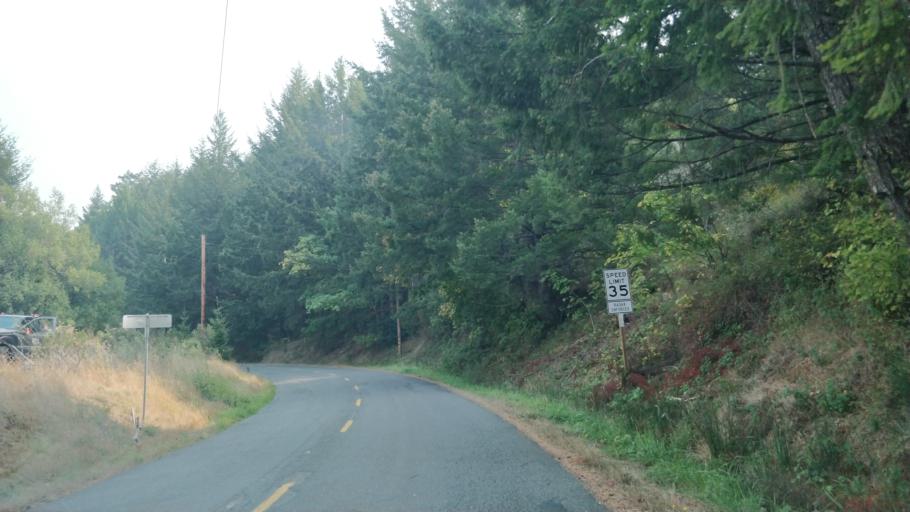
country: US
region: California
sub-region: Humboldt County
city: Rio Dell
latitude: 40.3127
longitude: -124.2830
